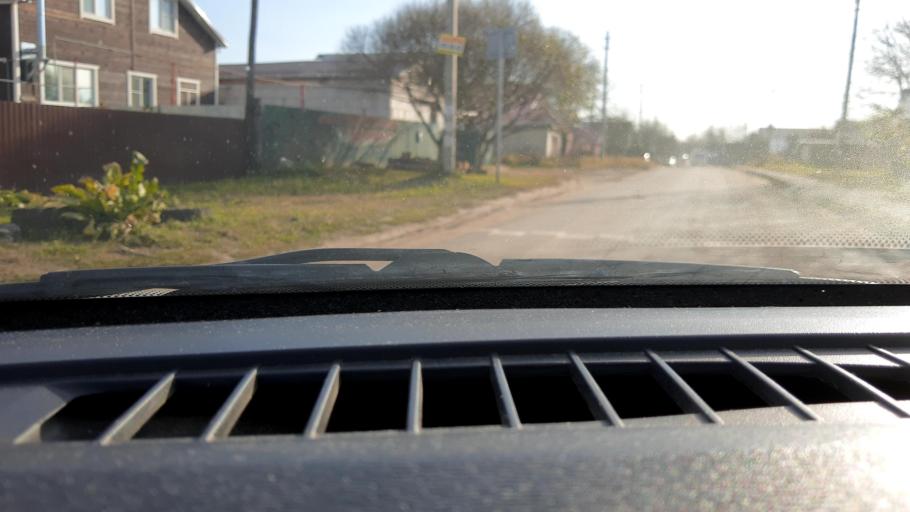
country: RU
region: Nizjnij Novgorod
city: Neklyudovo
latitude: 56.4132
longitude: 43.9796
